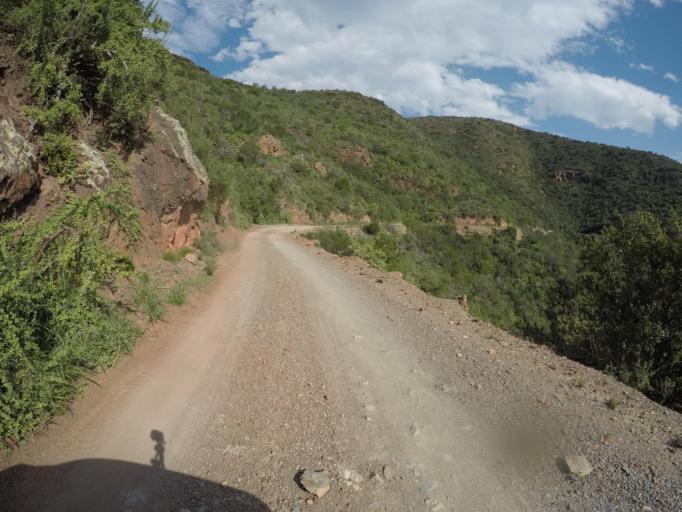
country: ZA
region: Eastern Cape
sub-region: Cacadu District Municipality
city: Kareedouw
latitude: -33.6481
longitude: 24.3444
